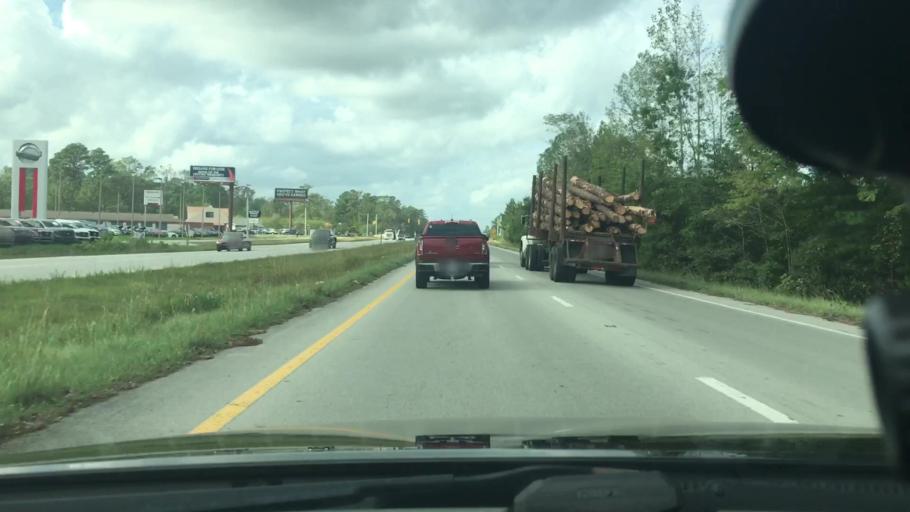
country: US
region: North Carolina
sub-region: Craven County
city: James City
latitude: 35.0478
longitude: -77.0128
